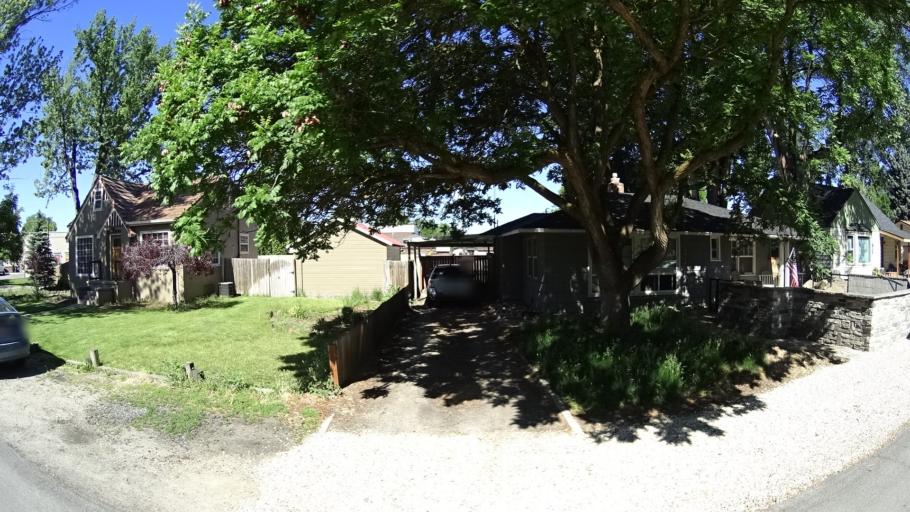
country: US
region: Idaho
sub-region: Ada County
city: Garden City
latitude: 43.6368
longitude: -116.2283
